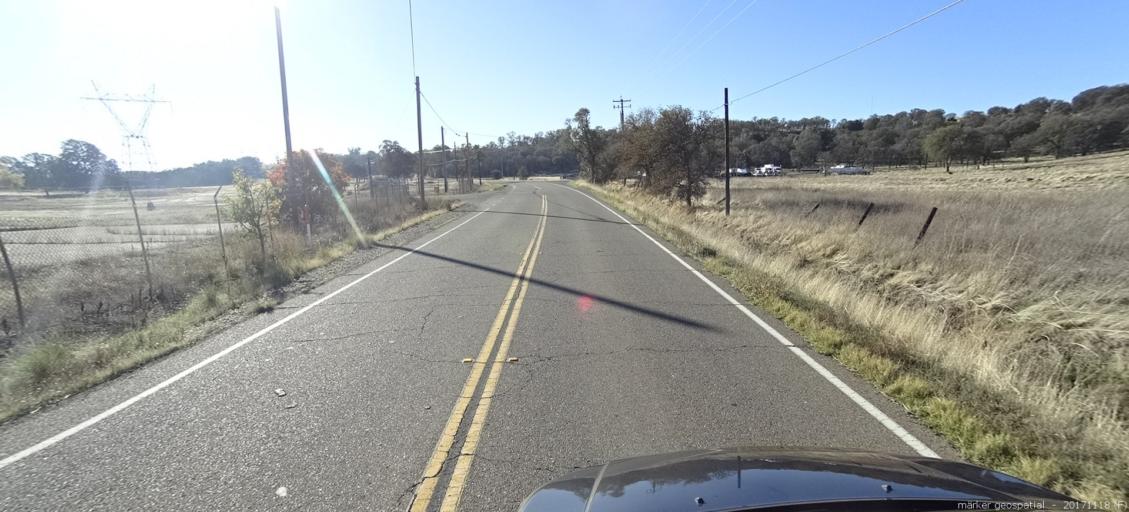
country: US
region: California
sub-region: Shasta County
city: Anderson
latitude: 40.4234
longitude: -122.2736
